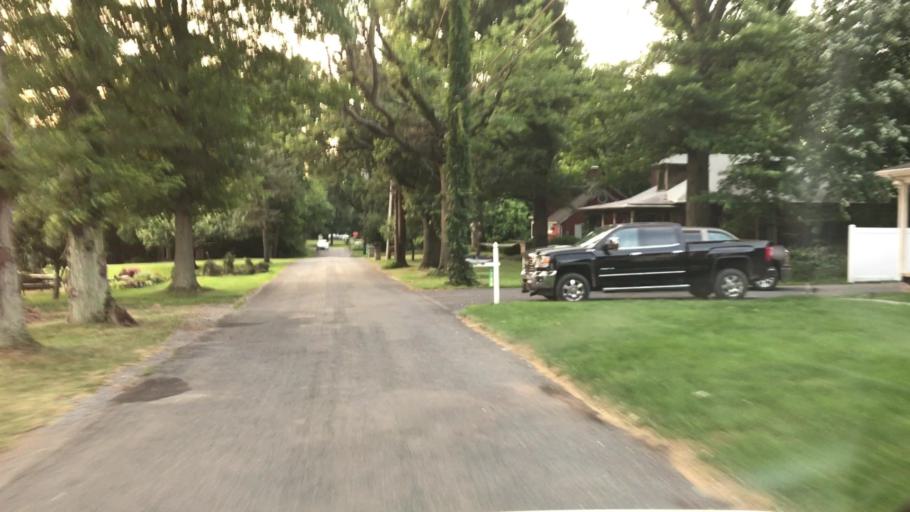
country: US
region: Pennsylvania
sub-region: Dauphin County
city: Middletown
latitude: 40.1803
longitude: -76.7265
